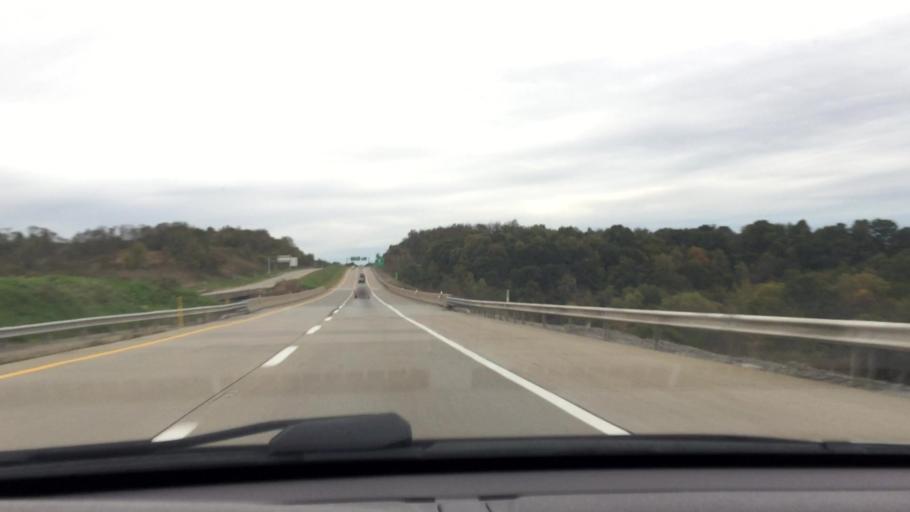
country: US
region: Pennsylvania
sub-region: Lawrence County
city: Oakland
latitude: 40.9563
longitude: -80.3947
